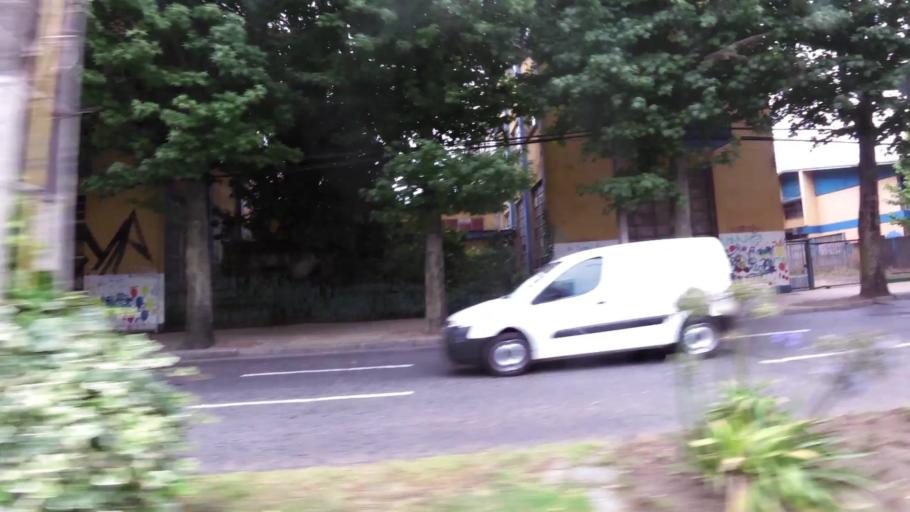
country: CL
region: Biobio
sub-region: Provincia de Concepcion
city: Concepcion
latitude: -36.8305
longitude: -73.0480
